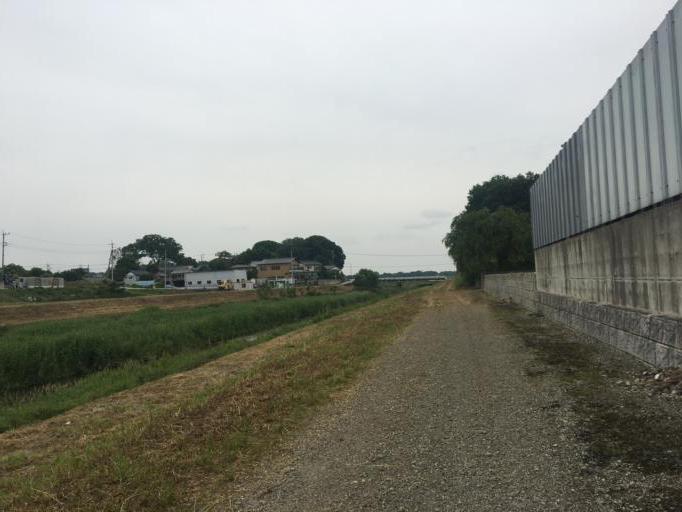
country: JP
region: Saitama
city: Sakado
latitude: 36.0046
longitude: 139.4394
